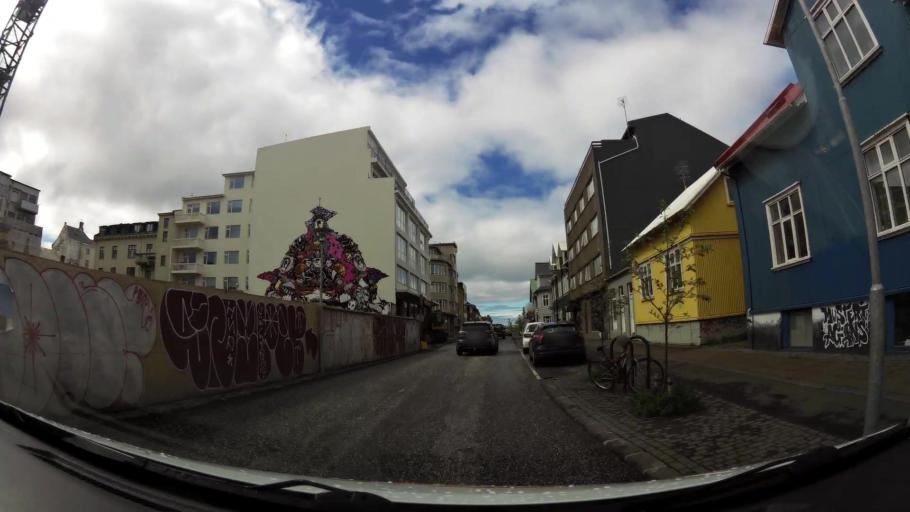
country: IS
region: Capital Region
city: Reykjavik
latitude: 64.1461
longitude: -21.9277
